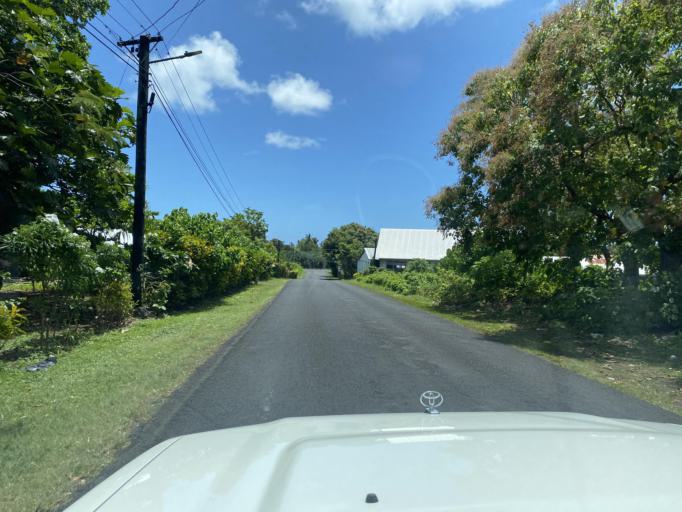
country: WS
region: Tuamasaga
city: Apia
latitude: -13.8386
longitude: -171.7571
